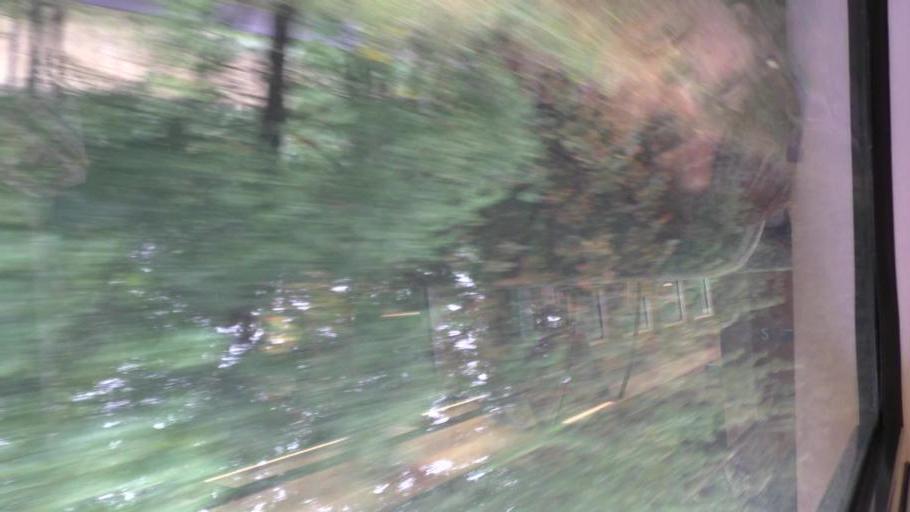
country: DE
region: Saxony
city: Neukirch/Lausitz
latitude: 51.0845
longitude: 14.2694
